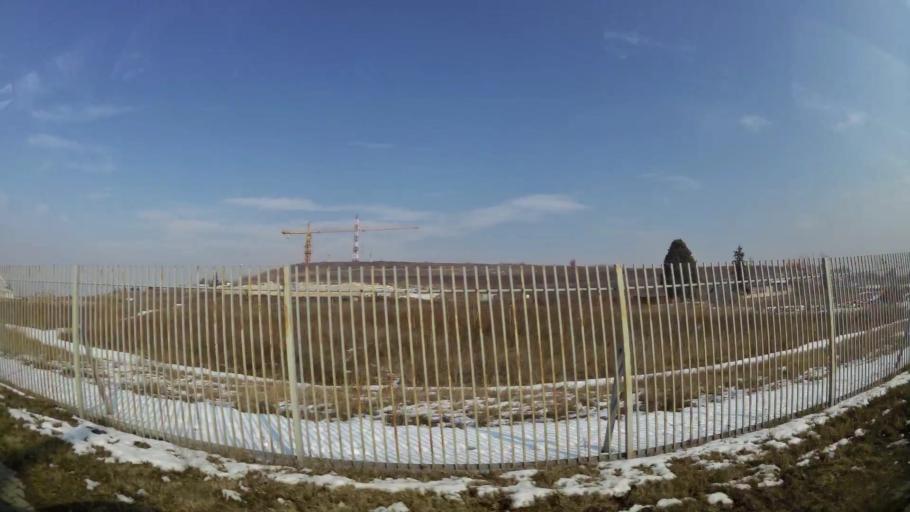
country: MK
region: Suto Orizari
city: Suto Orizare
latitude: 42.0156
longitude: 21.3930
